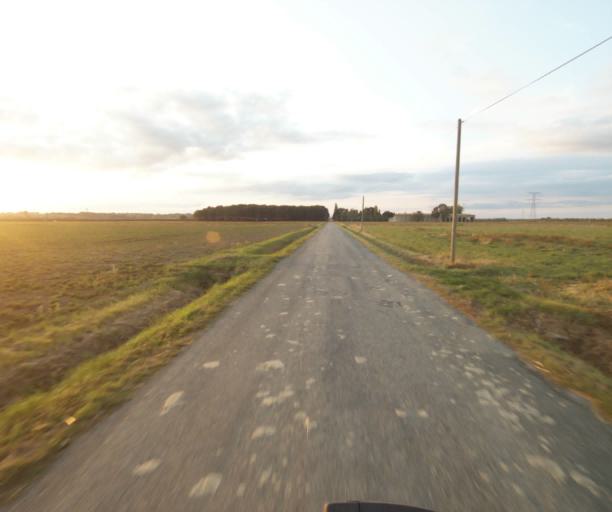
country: FR
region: Midi-Pyrenees
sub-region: Departement du Tarn-et-Garonne
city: Verdun-sur-Garonne
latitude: 43.8264
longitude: 1.2344
